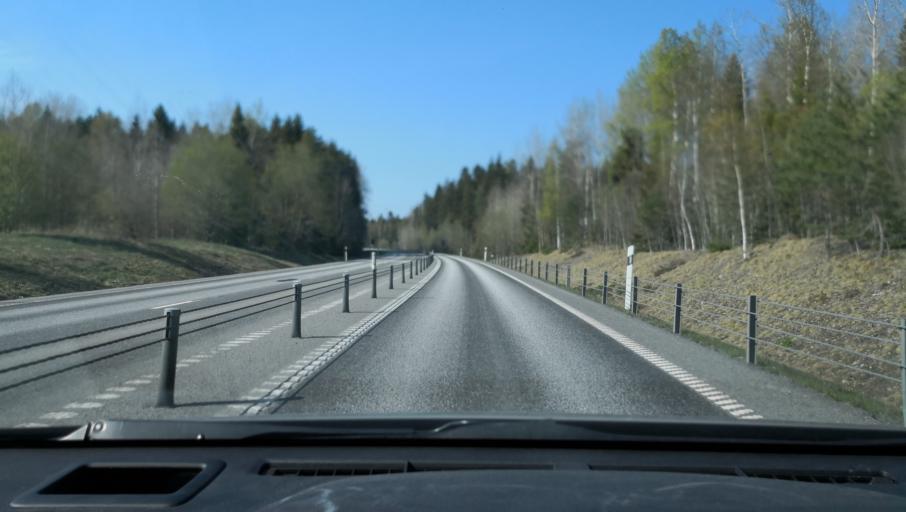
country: SE
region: Uppsala
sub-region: Heby Kommun
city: Tarnsjo
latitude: 60.1715
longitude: 16.9545
